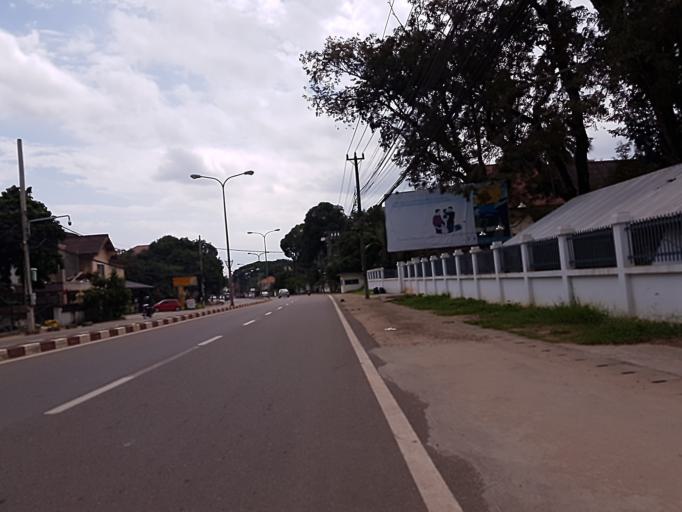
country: LA
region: Vientiane
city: Vientiane
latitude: 17.9347
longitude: 102.6168
